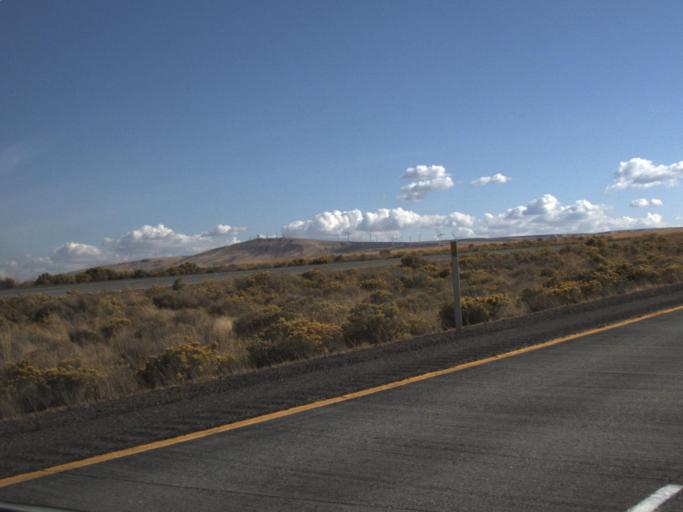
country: US
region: Washington
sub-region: Benton County
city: Kennewick
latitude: 46.1614
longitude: -119.2020
